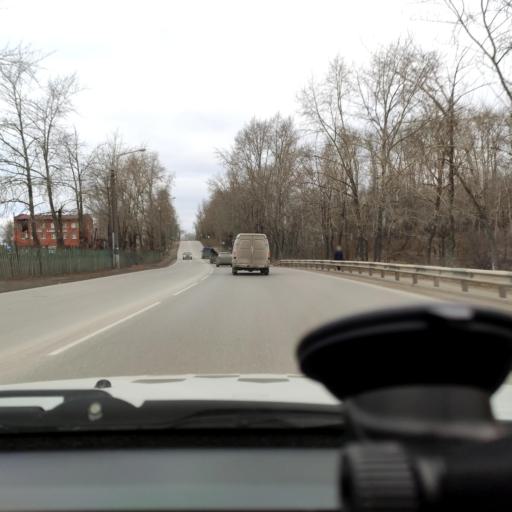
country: RU
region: Perm
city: Perm
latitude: 58.1161
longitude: 56.3678
